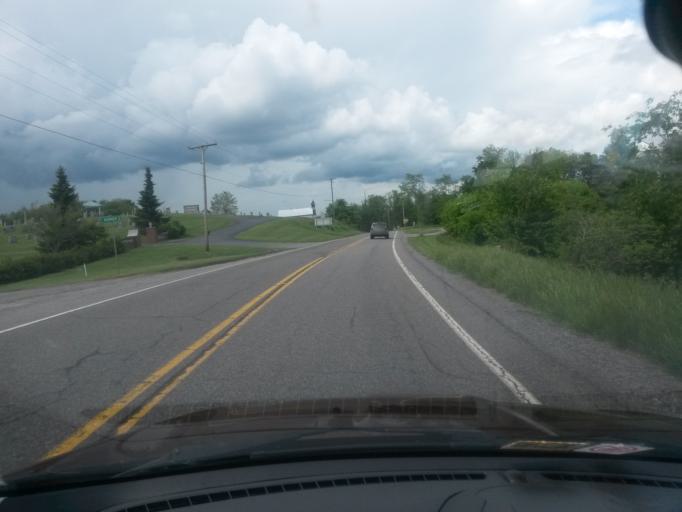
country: US
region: Virginia
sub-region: Floyd County
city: Floyd
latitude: 36.9057
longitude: -80.3176
